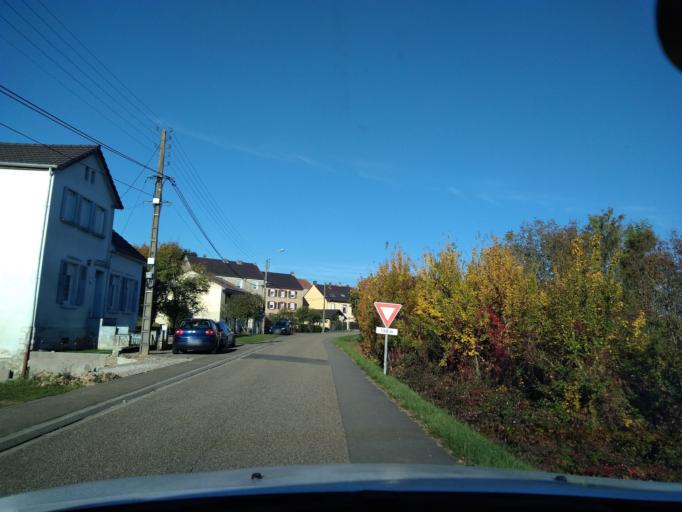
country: FR
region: Lorraine
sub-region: Departement de la Moselle
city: Remelfing
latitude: 49.0943
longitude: 7.0835
